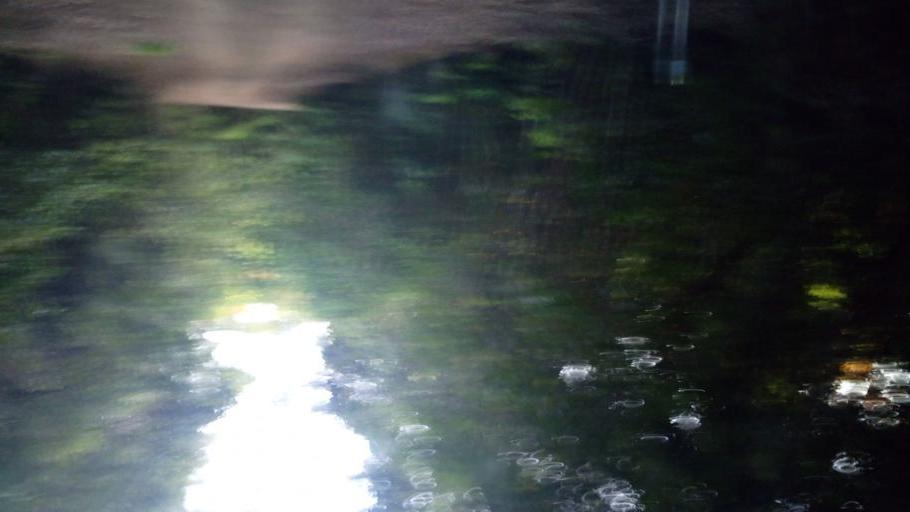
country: AU
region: Queensland
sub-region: Tablelands
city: Atherton
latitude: -17.3731
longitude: 145.7556
